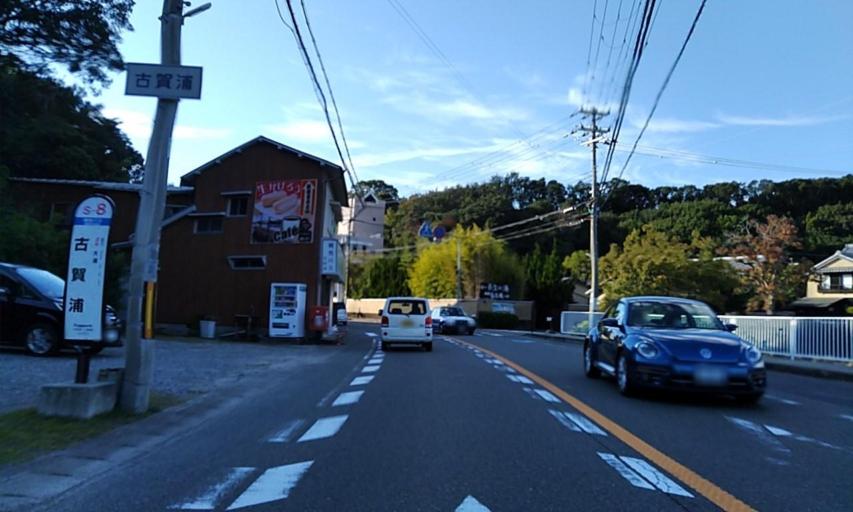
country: JP
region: Wakayama
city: Tanabe
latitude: 33.6802
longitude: 135.3584
